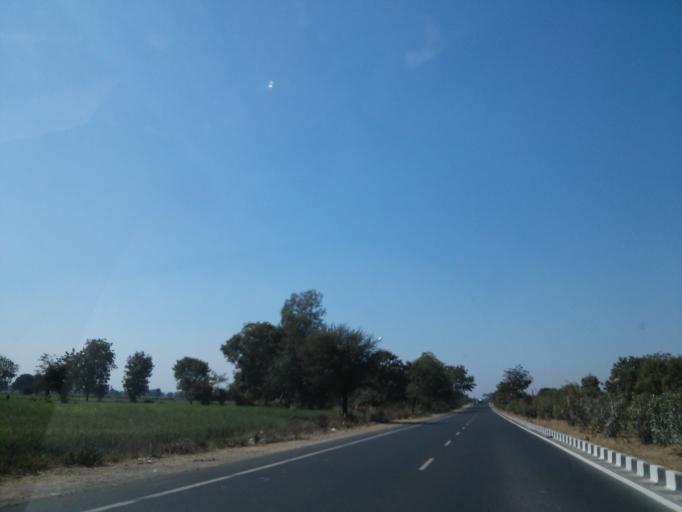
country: IN
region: Gujarat
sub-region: Sabar Kantha
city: Modasa
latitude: 23.6788
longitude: 73.3548
